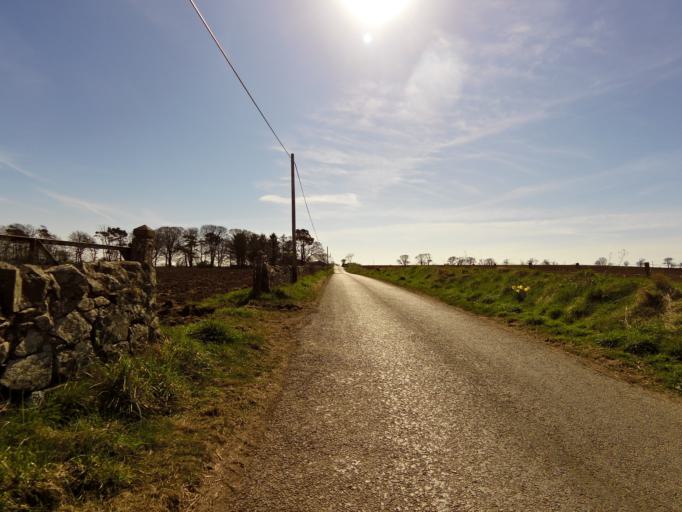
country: GB
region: Scotland
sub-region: Angus
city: Montrose
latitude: 56.6871
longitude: -2.4588
